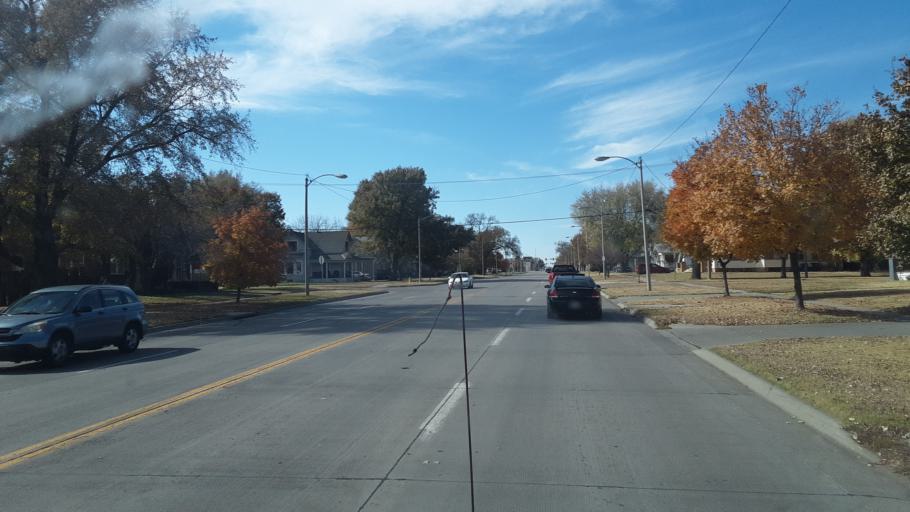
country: US
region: Kansas
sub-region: McPherson County
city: McPherson
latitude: 38.3694
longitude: -97.6587
